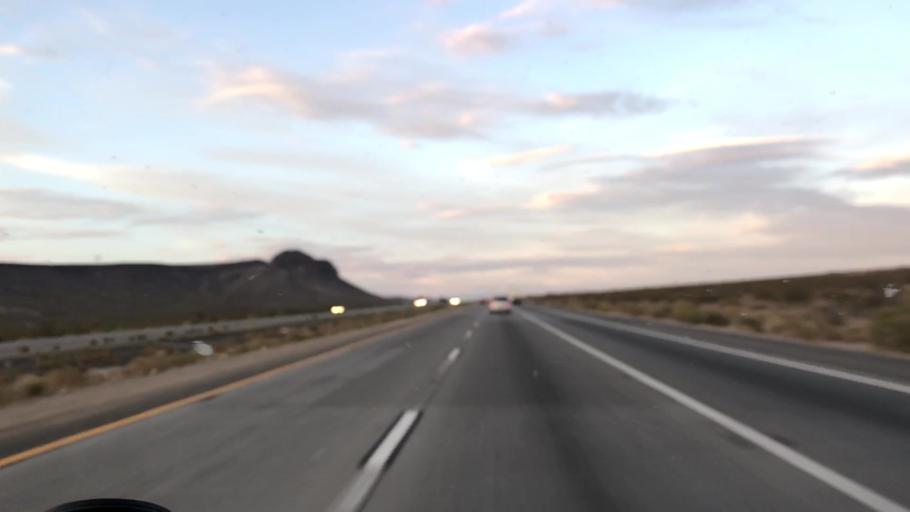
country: US
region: Nevada
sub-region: Clark County
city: Sandy Valley
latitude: 35.3853
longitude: -115.8556
